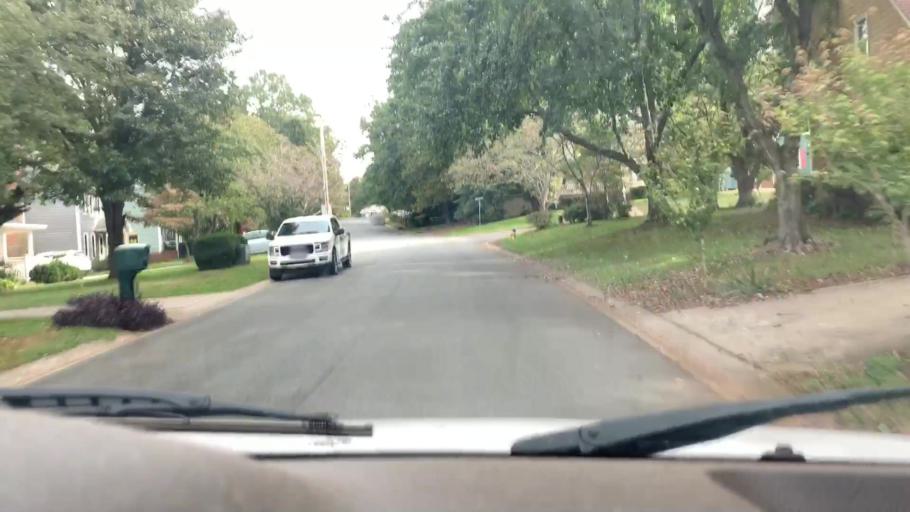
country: US
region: North Carolina
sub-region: Mecklenburg County
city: Cornelius
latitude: 35.4756
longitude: -80.8582
